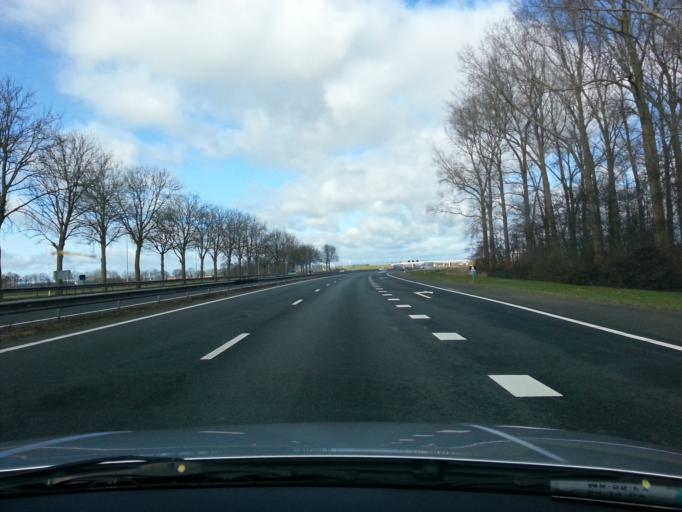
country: NL
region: Gelderland
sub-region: Gemeente Nijkerk
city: Nijkerk
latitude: 52.2047
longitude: 5.4397
